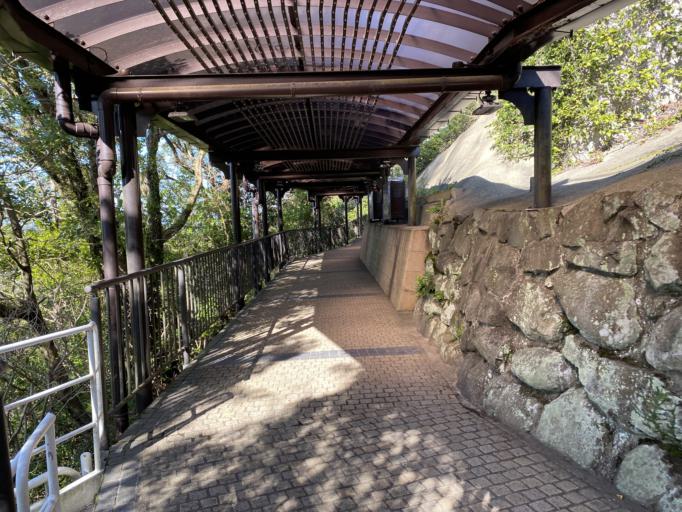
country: JP
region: Nagasaki
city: Nagasaki-shi
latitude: 32.7537
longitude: 129.8492
